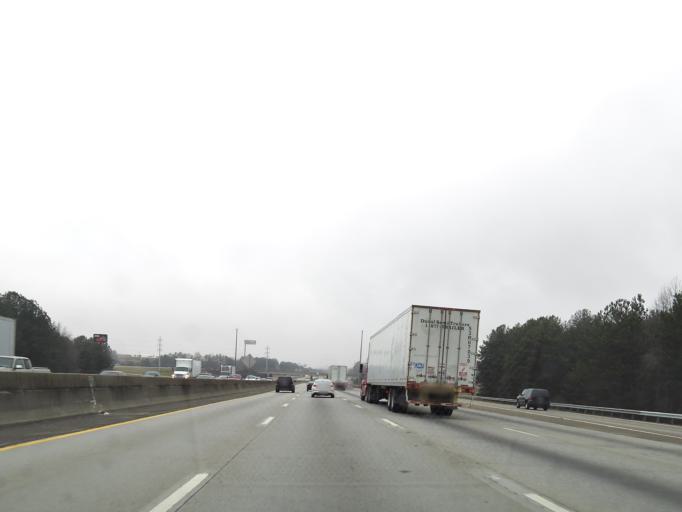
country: US
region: Georgia
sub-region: Clayton County
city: Morrow
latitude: 33.5620
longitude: -84.3152
